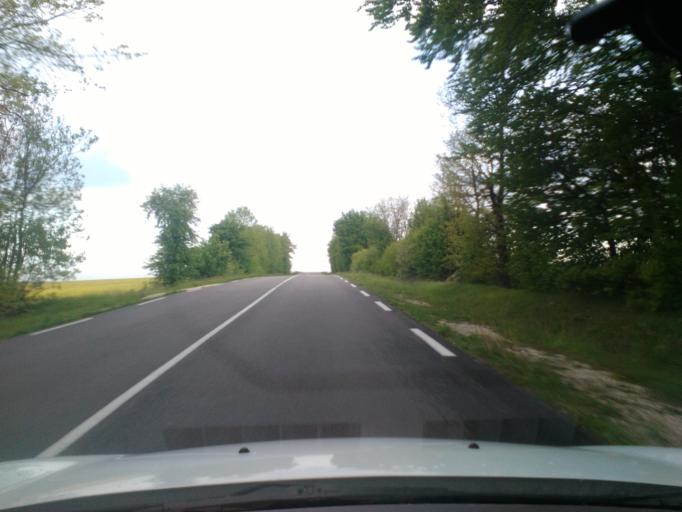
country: FR
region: Champagne-Ardenne
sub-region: Departement de la Haute-Marne
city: Lavilleneuve-au-Roi
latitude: 48.1949
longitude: 4.9505
